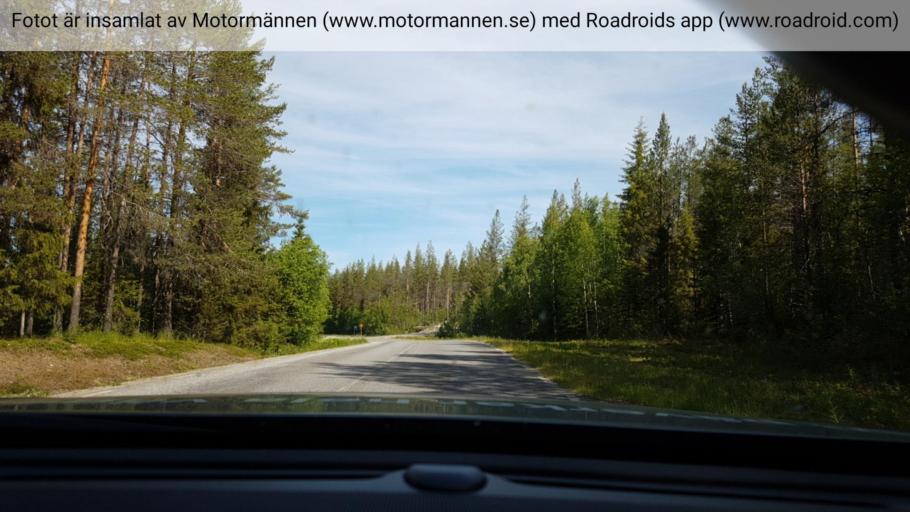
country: SE
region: Vaesterbotten
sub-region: Vilhelmina Kommun
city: Sjoberg
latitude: 64.5863
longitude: 15.8707
